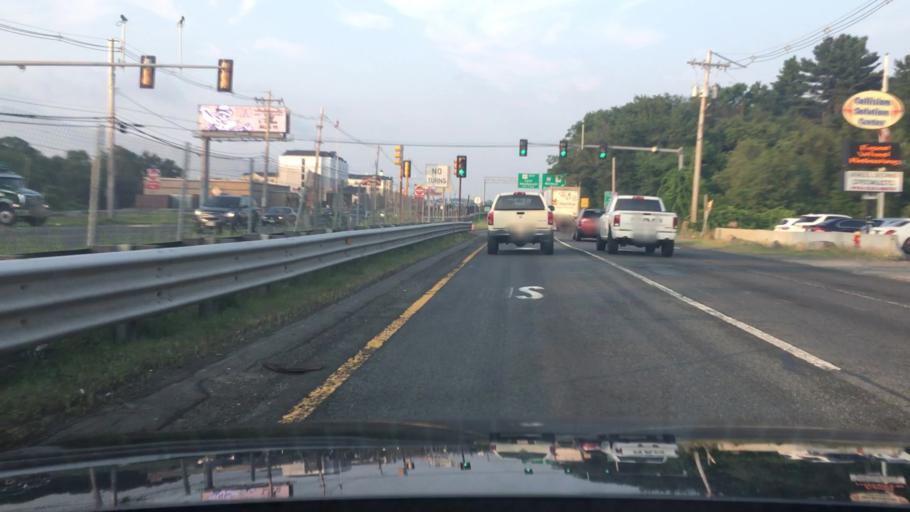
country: US
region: Massachusetts
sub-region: Essex County
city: South Peabody
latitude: 42.5295
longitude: -70.9930
